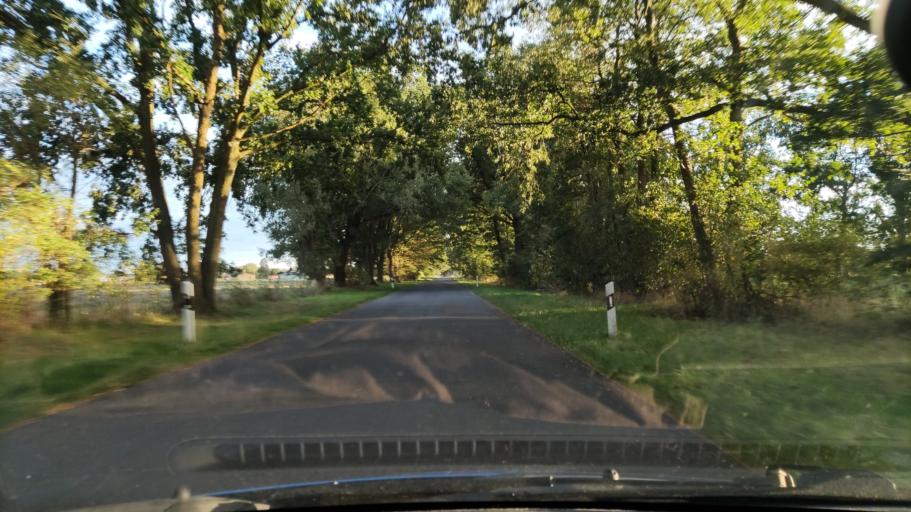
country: DE
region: Lower Saxony
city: Neu Darchau
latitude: 53.3493
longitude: 10.8638
